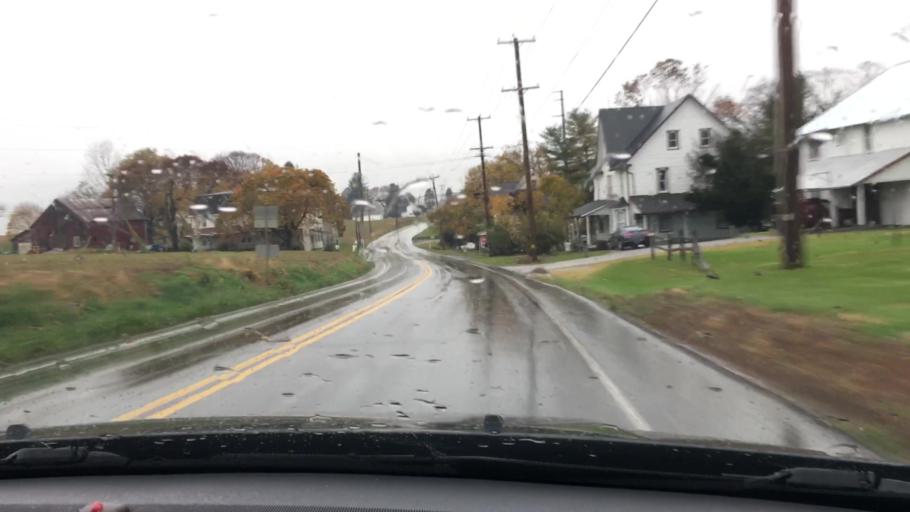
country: US
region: Pennsylvania
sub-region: York County
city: Susquehanna Trails
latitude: 39.8181
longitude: -76.3866
